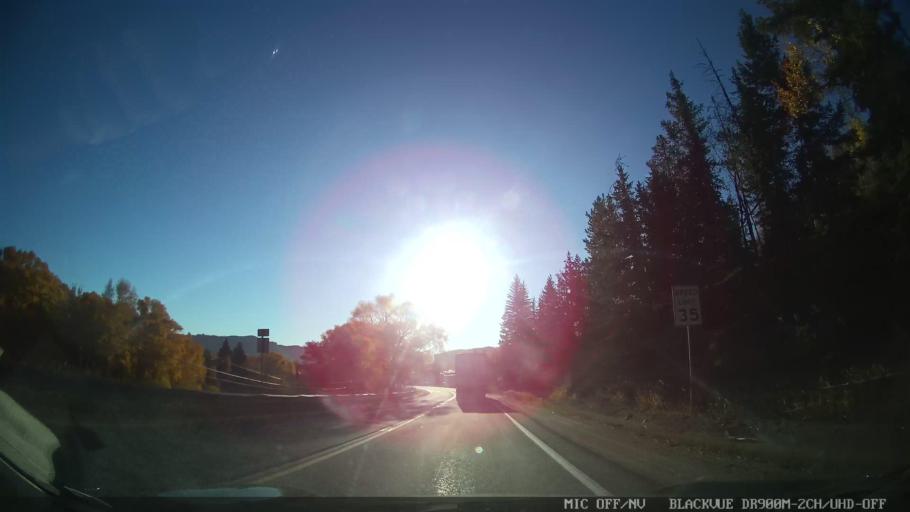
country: US
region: Colorado
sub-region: Grand County
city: Hot Sulphur Springs
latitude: 40.0734
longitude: -106.1102
